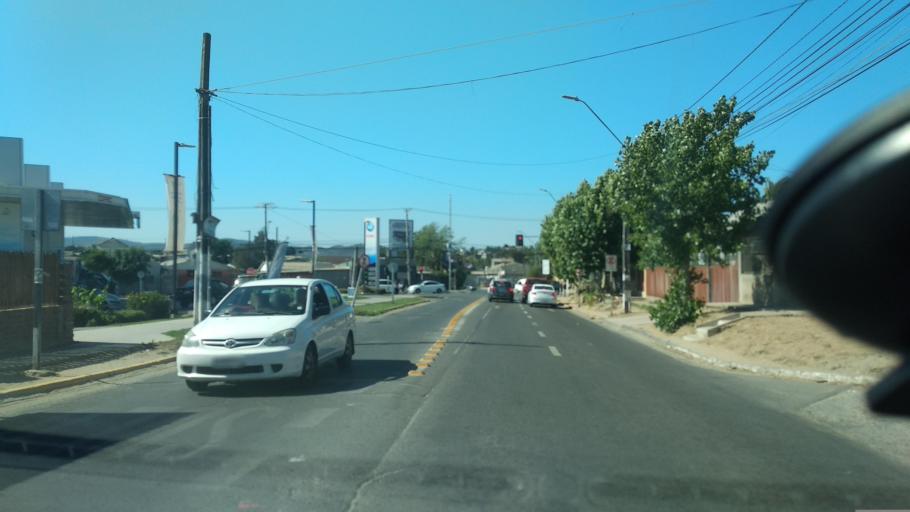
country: CL
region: Valparaiso
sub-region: Provincia de Marga Marga
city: Villa Alemana
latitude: -33.0596
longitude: -71.3725
